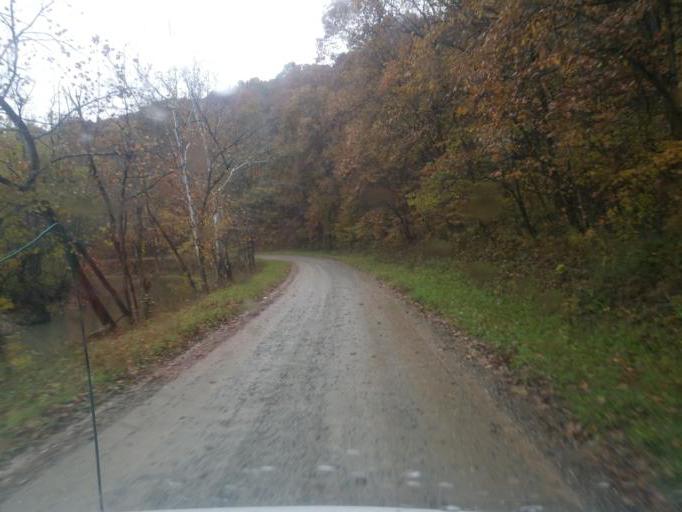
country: US
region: Ohio
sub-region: Washington County
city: Beverly
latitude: 39.4802
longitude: -81.7383
